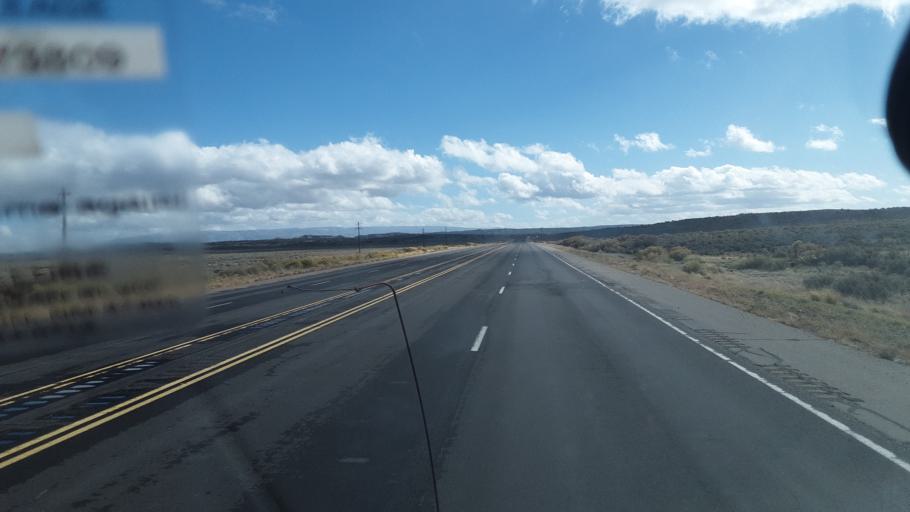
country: US
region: New Mexico
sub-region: Rio Arriba County
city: Santa Teresa
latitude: 36.1322
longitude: -107.2186
